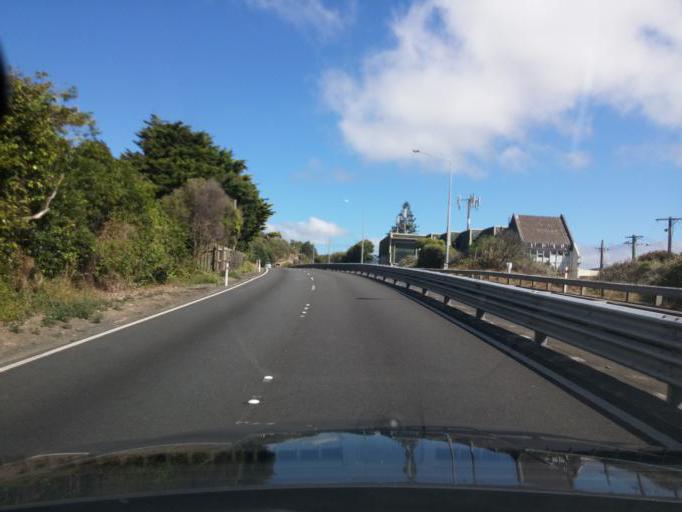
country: NZ
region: Wellington
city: Petone
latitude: -41.2218
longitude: 174.8090
